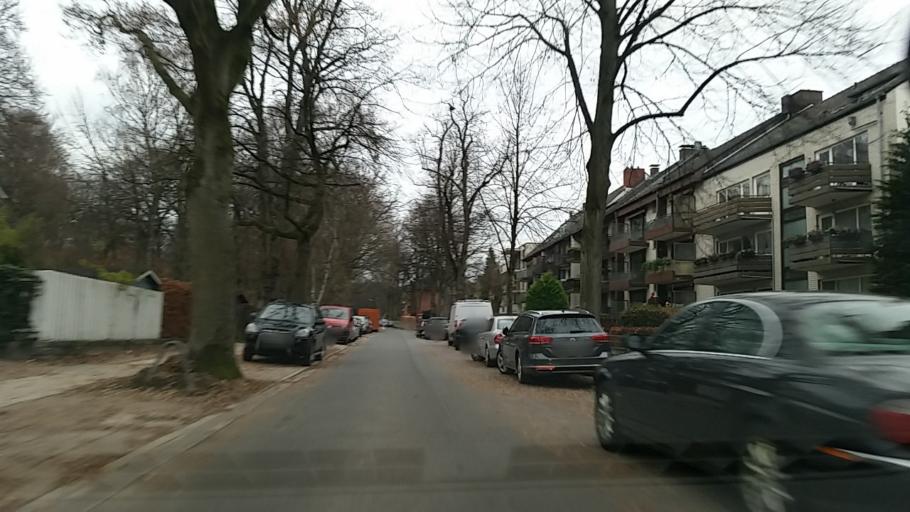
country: DE
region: Hamburg
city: Altona
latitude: 53.5664
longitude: 9.9027
